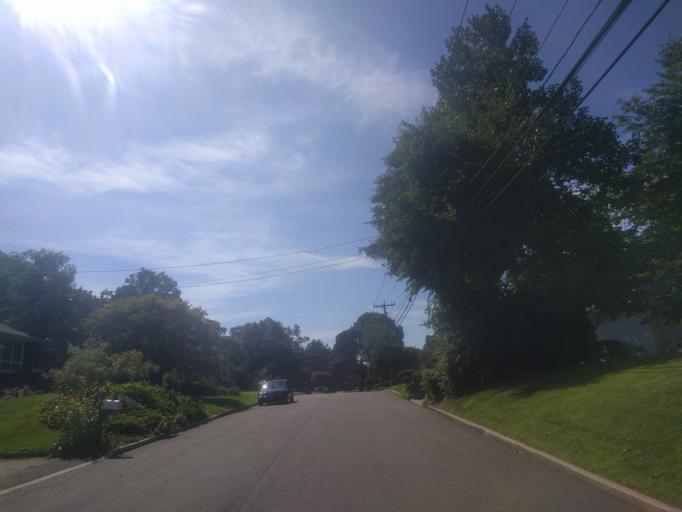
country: US
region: New York
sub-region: Nassau County
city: Glen Cove
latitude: 40.8823
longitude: -73.6227
